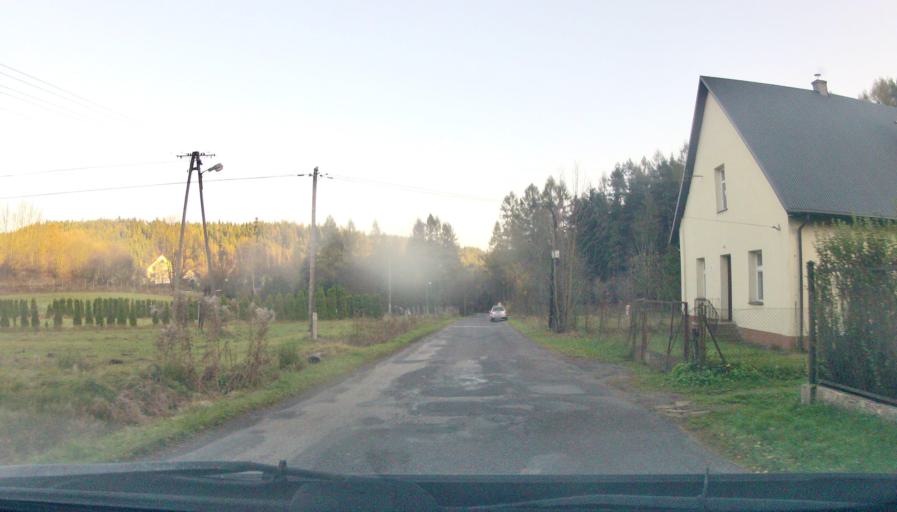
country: PL
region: Lesser Poland Voivodeship
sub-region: Powiat suski
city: Krzeszow
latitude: 49.7623
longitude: 19.4534
